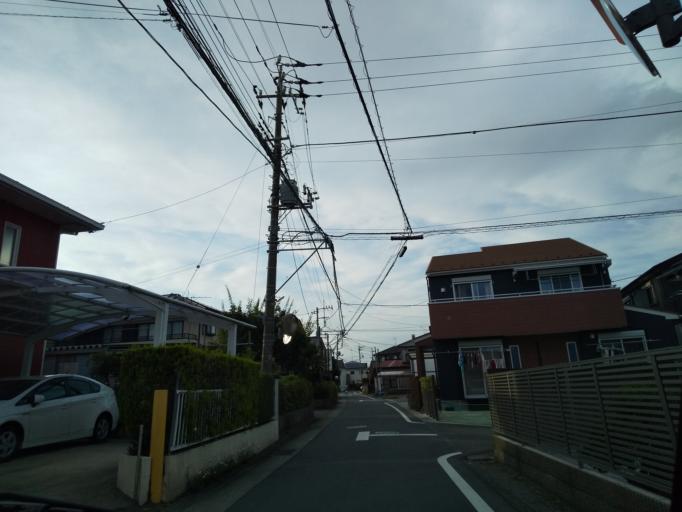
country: JP
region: Kanagawa
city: Zama
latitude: 35.5070
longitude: 139.3617
